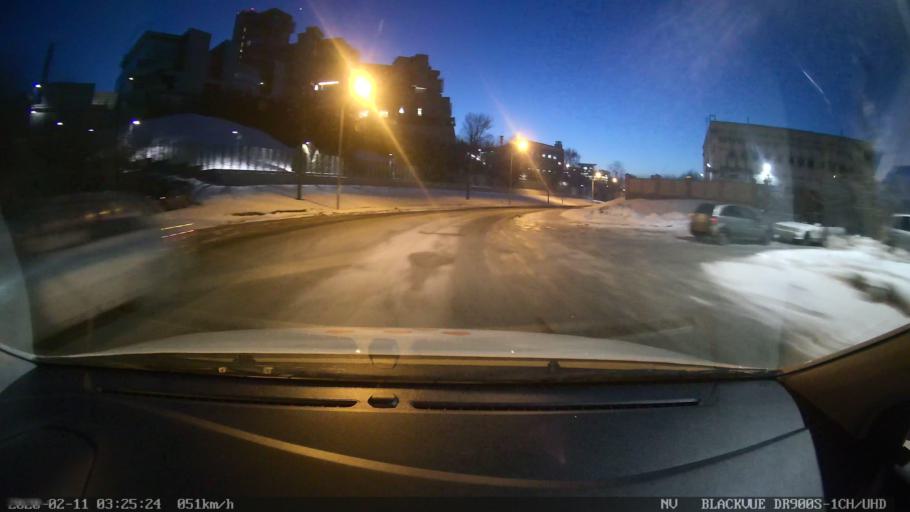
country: RU
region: Tatarstan
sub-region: Gorod Kazan'
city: Kazan
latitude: 55.8019
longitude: 49.1363
